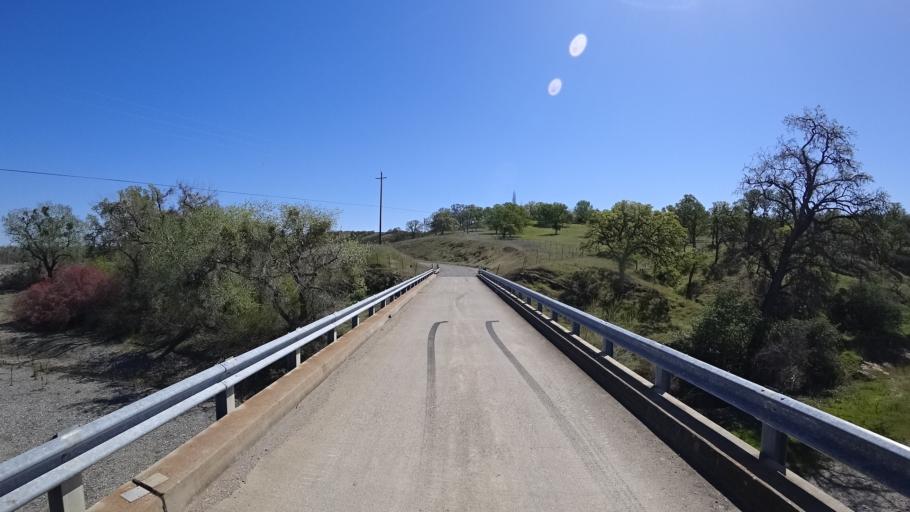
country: US
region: California
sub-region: Glenn County
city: Orland
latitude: 39.7317
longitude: -122.4137
